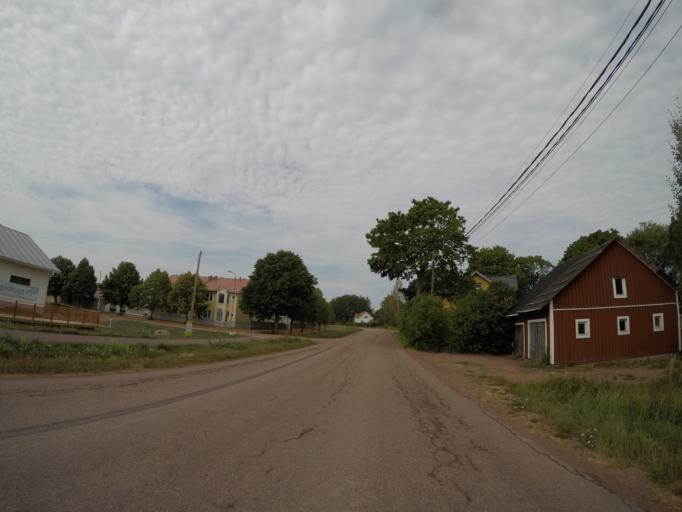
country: AX
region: Alands landsbygd
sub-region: Finstroem
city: Finstroem
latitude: 60.2322
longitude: 19.9950
